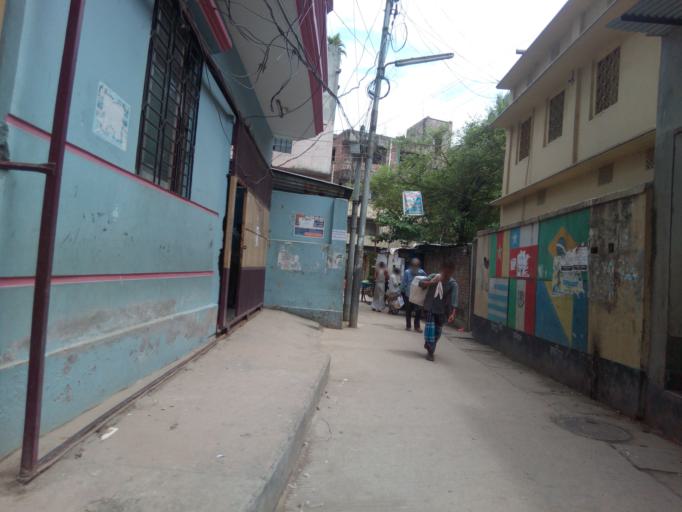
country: BD
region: Dhaka
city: Azimpur
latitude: 23.7283
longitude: 90.3725
